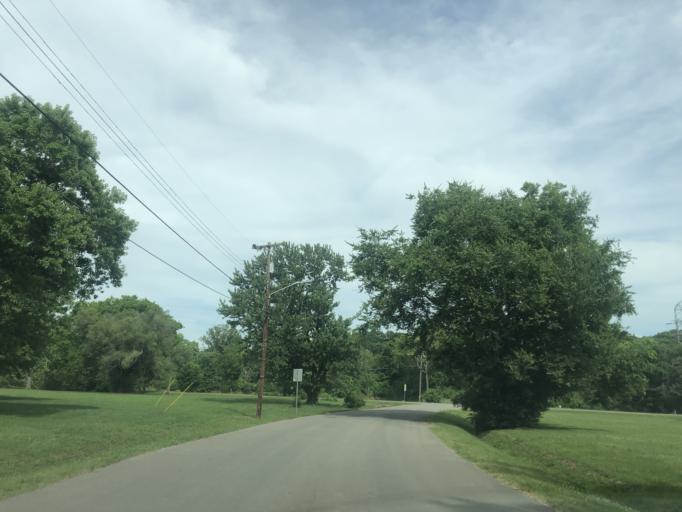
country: US
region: Tennessee
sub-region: Davidson County
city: Nashville
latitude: 36.2166
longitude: -86.8231
